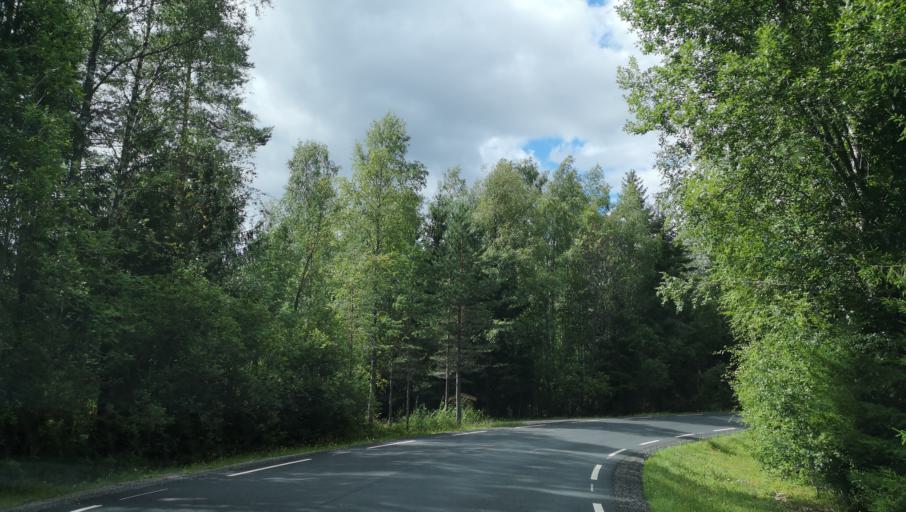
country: NO
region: Ostfold
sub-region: Hobol
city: Tomter
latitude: 59.6807
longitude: 10.9425
